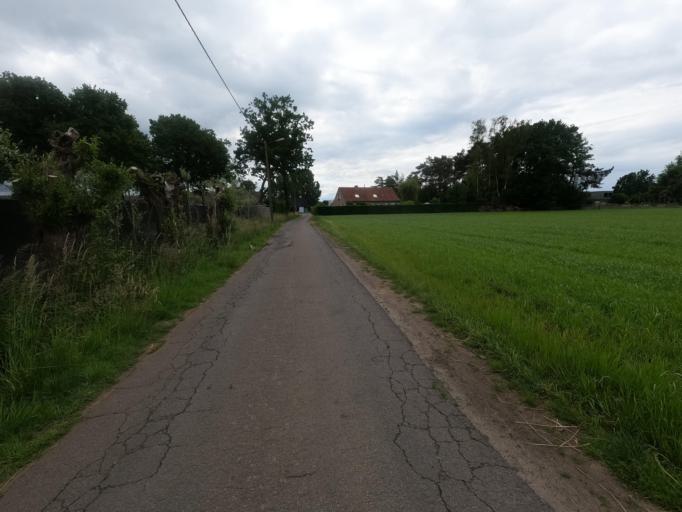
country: BE
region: Flanders
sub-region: Provincie Antwerpen
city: Heist-op-den-Berg
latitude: 51.0462
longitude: 4.6983
